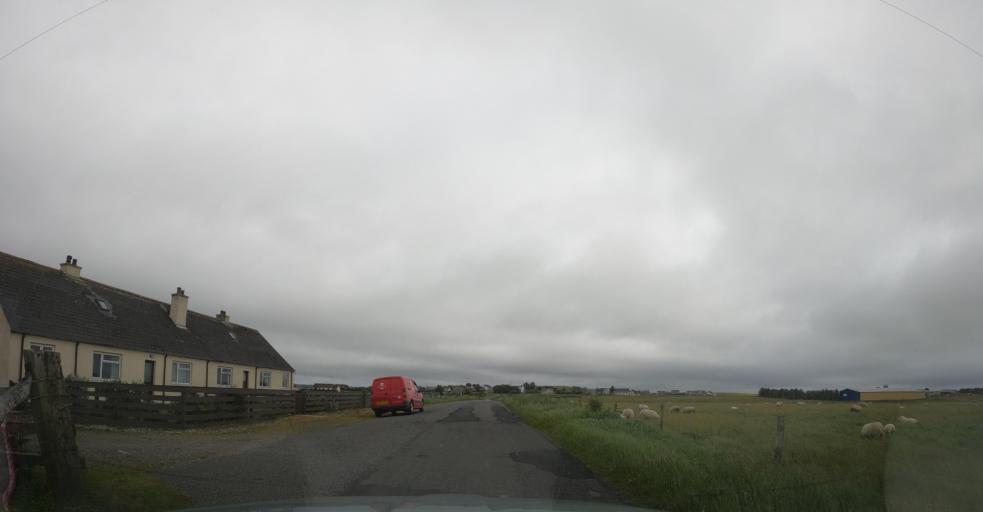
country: GB
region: Scotland
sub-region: Eilean Siar
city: Stornoway
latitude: 58.1988
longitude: -6.3502
